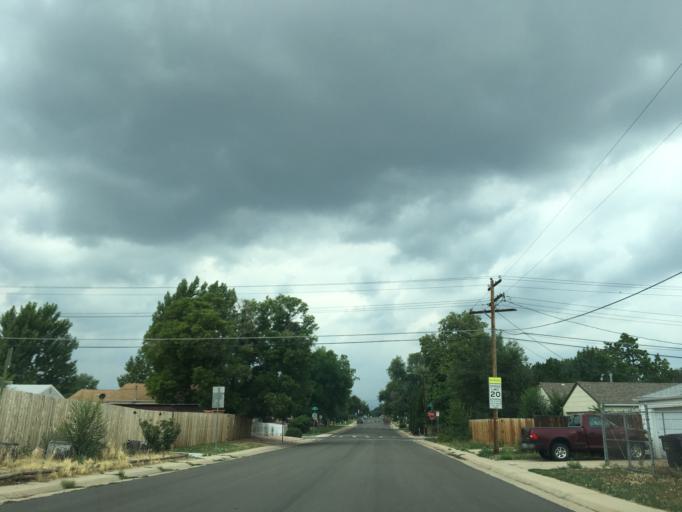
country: US
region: Colorado
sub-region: Arapahoe County
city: Sheridan
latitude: 39.6842
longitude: -105.0101
